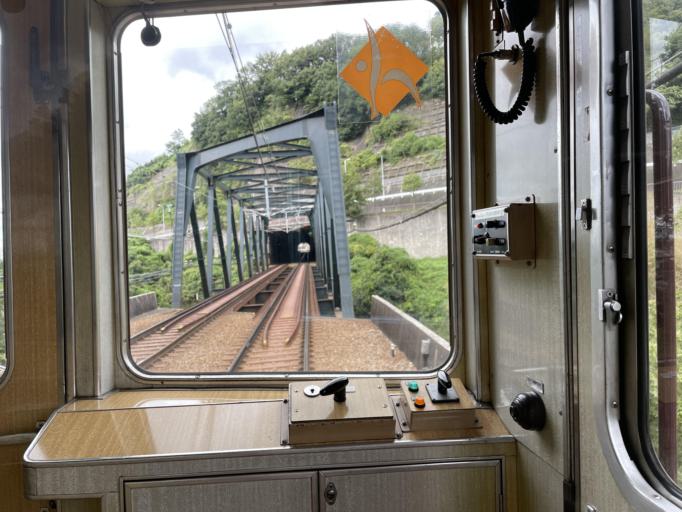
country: JP
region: Osaka
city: Ikeda
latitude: 34.8510
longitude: 135.4176
